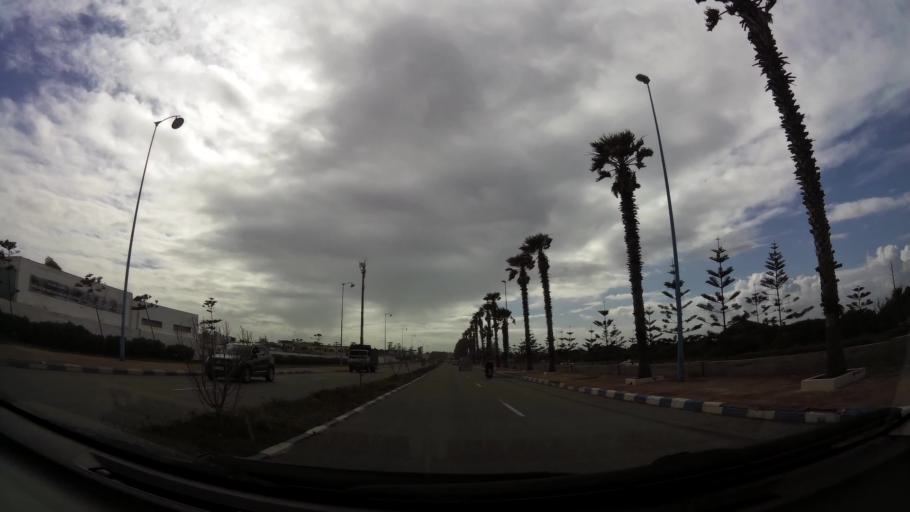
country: MA
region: Doukkala-Abda
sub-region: El-Jadida
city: El Jadida
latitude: 33.2440
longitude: -8.4671
